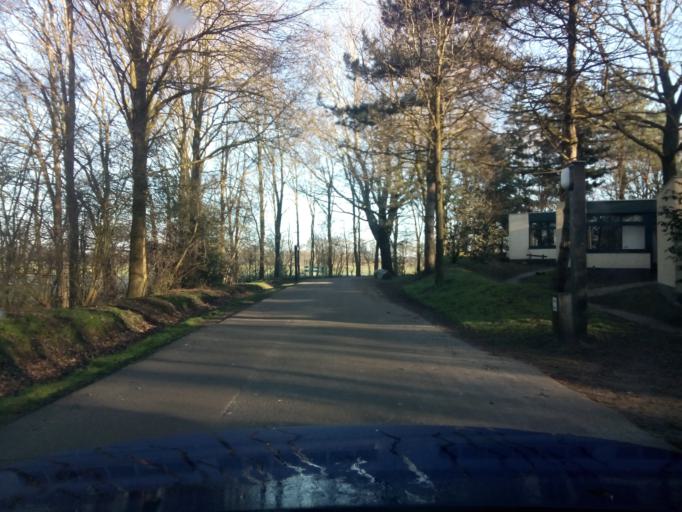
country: NL
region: Drenthe
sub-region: Gemeente Coevorden
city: Dalen
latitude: 52.6760
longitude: 6.7618
